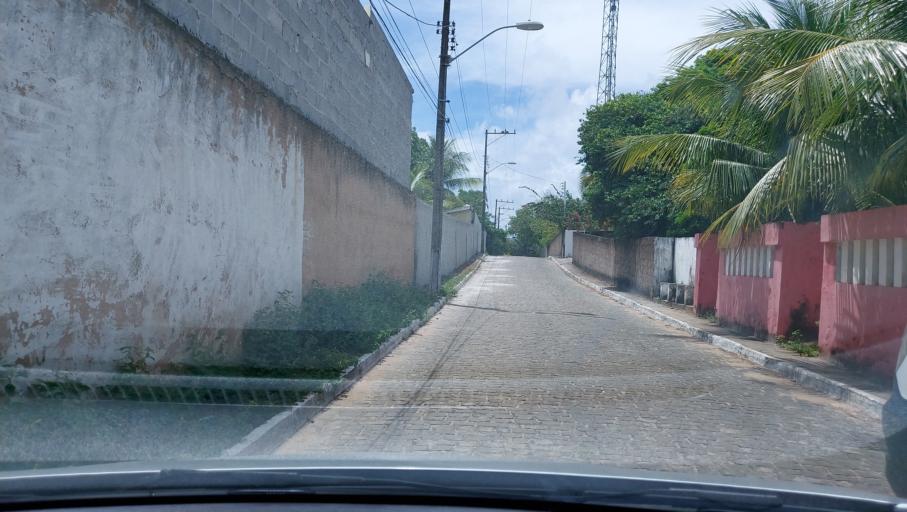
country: BR
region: Bahia
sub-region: Mata De Sao Joao
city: Mata de Sao Joao
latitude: -12.6270
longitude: -38.0472
